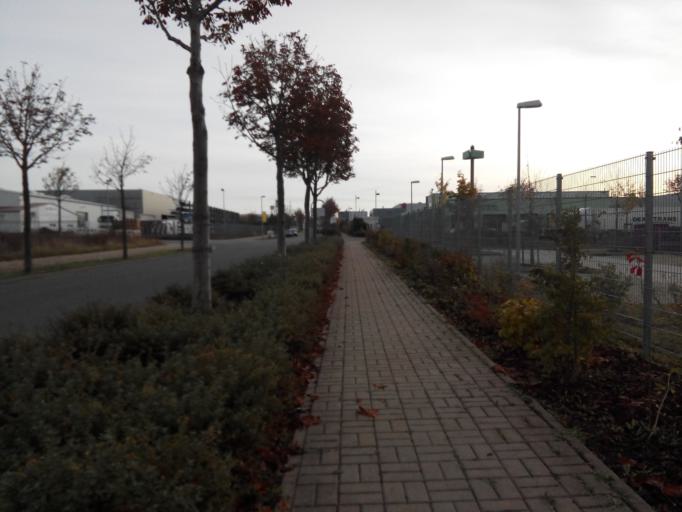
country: DE
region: Thuringia
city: Monchenholzhausen
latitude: 50.9775
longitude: 11.1181
